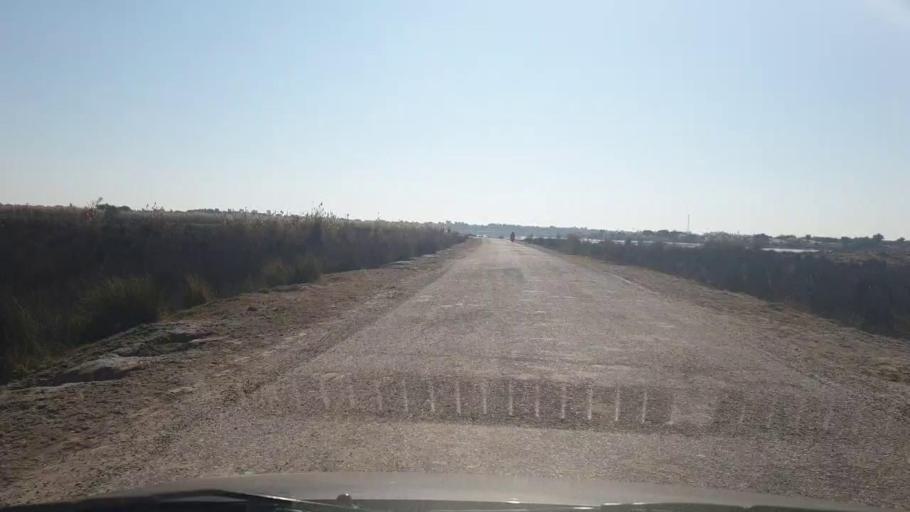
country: PK
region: Sindh
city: Bozdar
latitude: 27.1622
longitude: 68.6452
